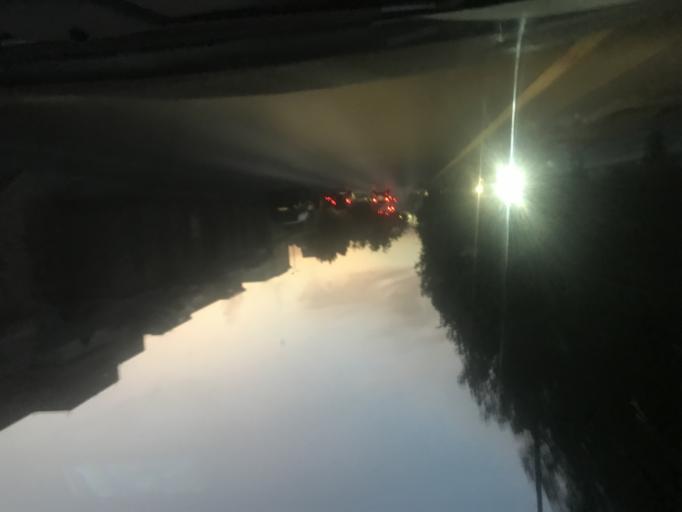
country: SA
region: Ar Riyad
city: Riyadh
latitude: 24.7292
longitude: 46.7589
